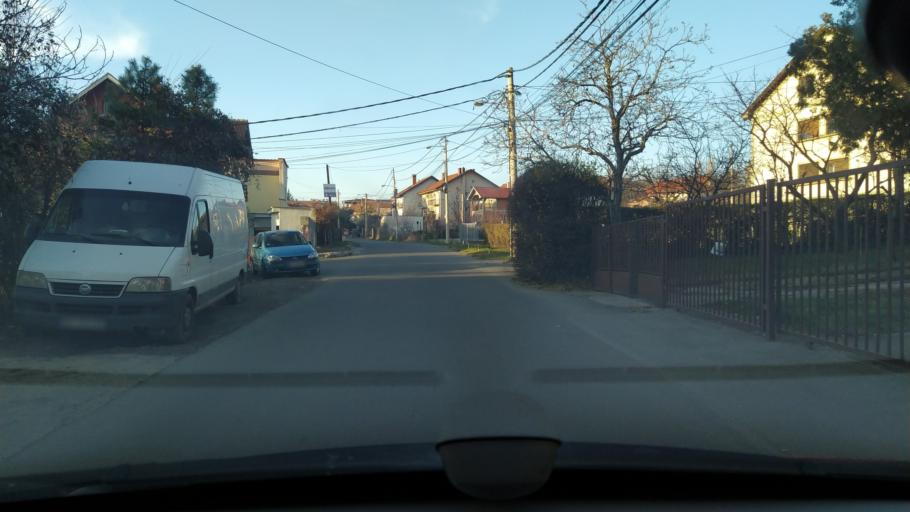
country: RS
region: Central Serbia
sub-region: Belgrade
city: Zvezdara
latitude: 44.7629
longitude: 20.5627
